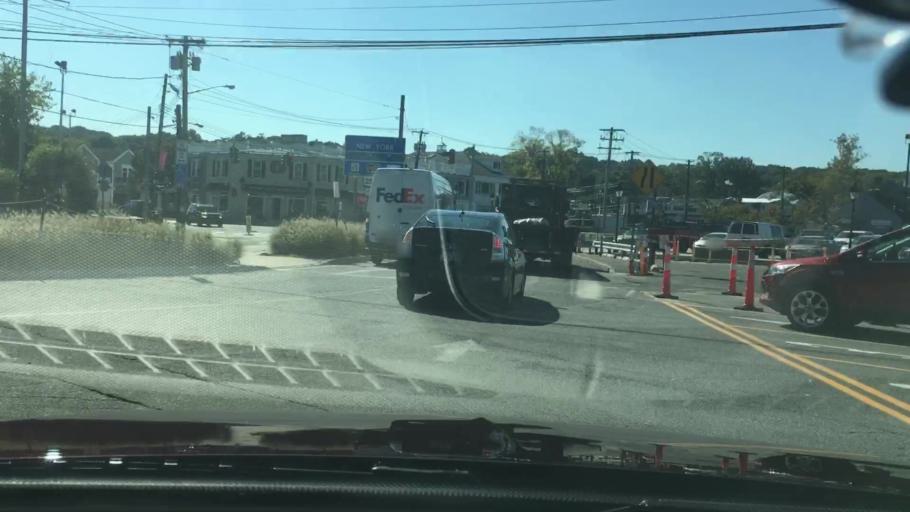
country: US
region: New York
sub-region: Suffolk County
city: Port Jefferson
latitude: 40.9473
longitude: -73.0694
